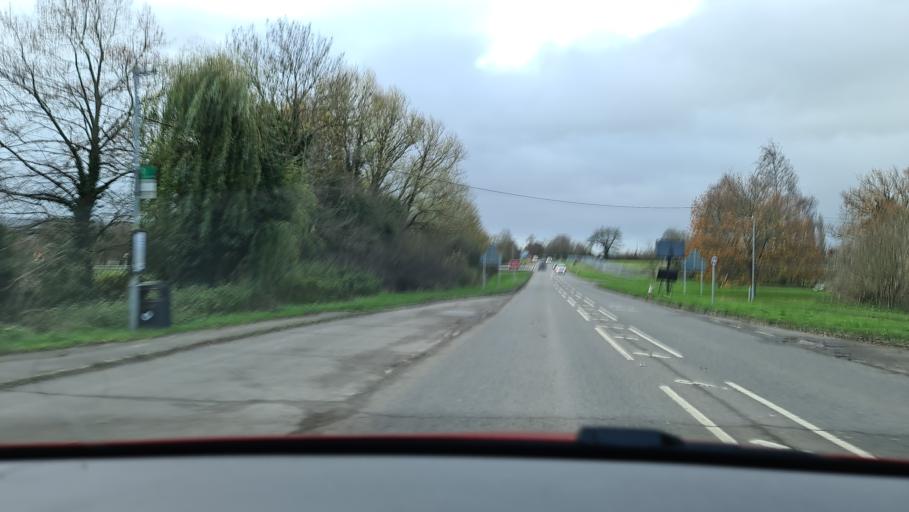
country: GB
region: England
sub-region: Buckinghamshire
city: Weston Turville
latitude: 51.7809
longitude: -0.7904
